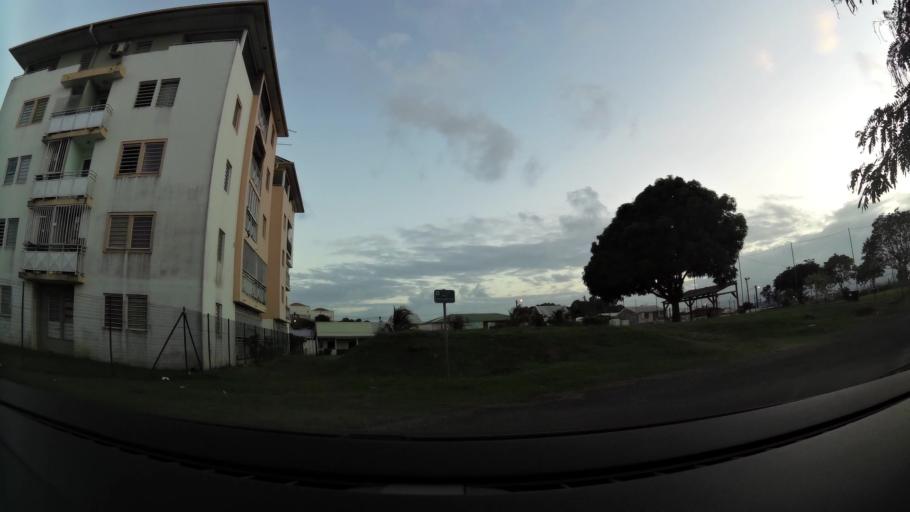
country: GP
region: Guadeloupe
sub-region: Guadeloupe
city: Les Abymes
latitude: 16.2775
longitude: -61.5055
